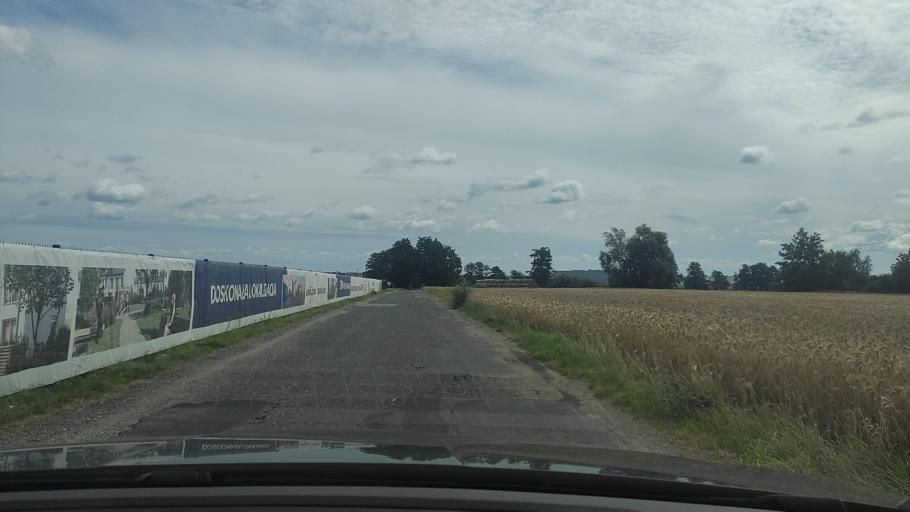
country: PL
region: Greater Poland Voivodeship
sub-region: Powiat poznanski
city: Kostrzyn
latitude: 52.4081
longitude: 17.1921
